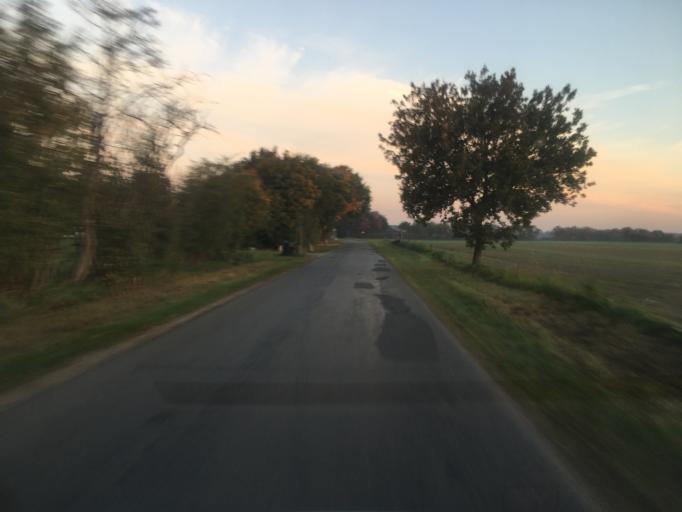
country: DE
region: Schleswig-Holstein
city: Bramstedtlund
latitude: 54.9806
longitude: 9.0666
